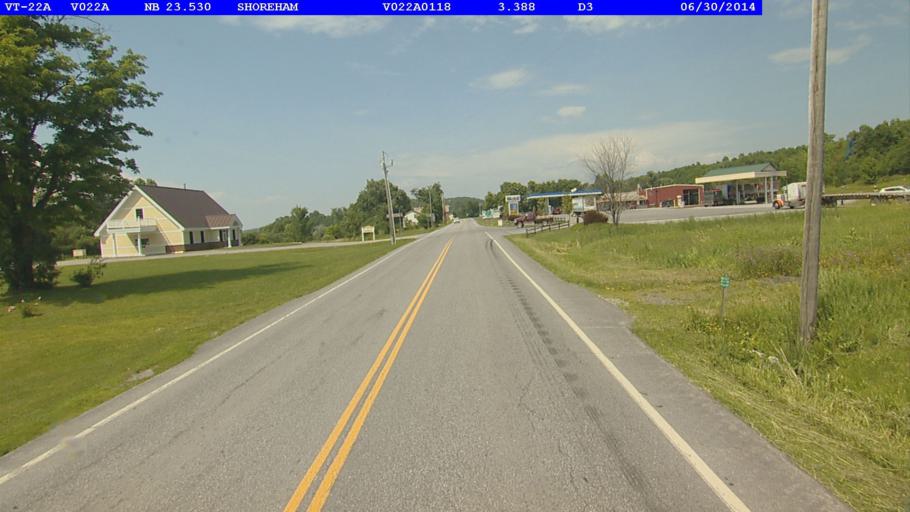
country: US
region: New York
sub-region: Essex County
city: Ticonderoga
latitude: 43.8984
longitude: -73.3085
